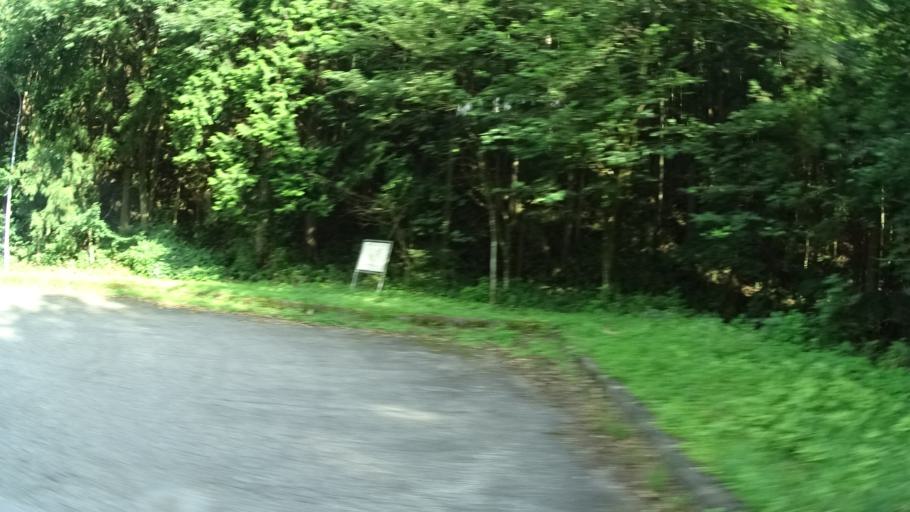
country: JP
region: Tochigi
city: Nikko
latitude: 36.7255
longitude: 139.5444
